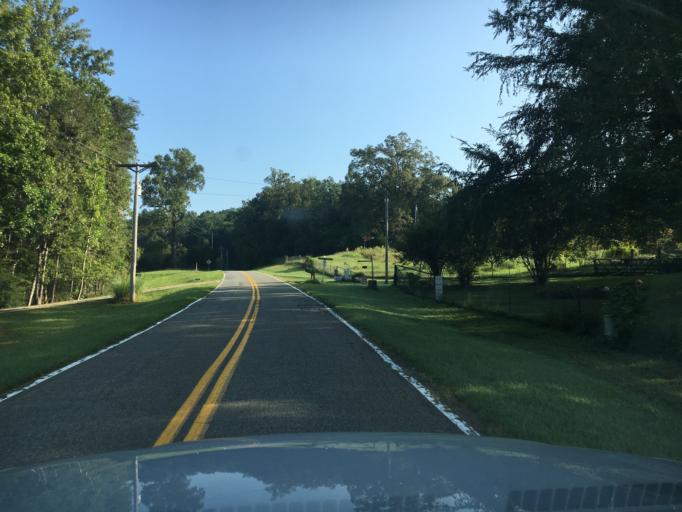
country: US
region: North Carolina
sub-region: Rutherford County
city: Rutherfordton
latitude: 35.2699
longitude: -82.0317
